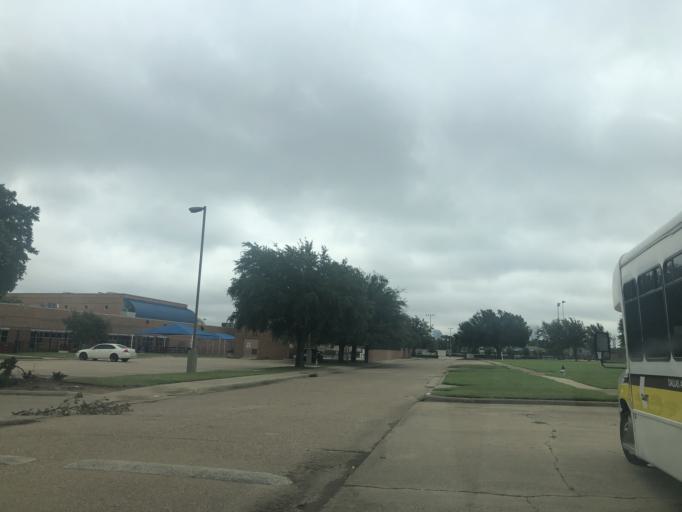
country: US
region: Texas
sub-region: Dallas County
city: Dallas
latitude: 32.7859
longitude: -96.8601
